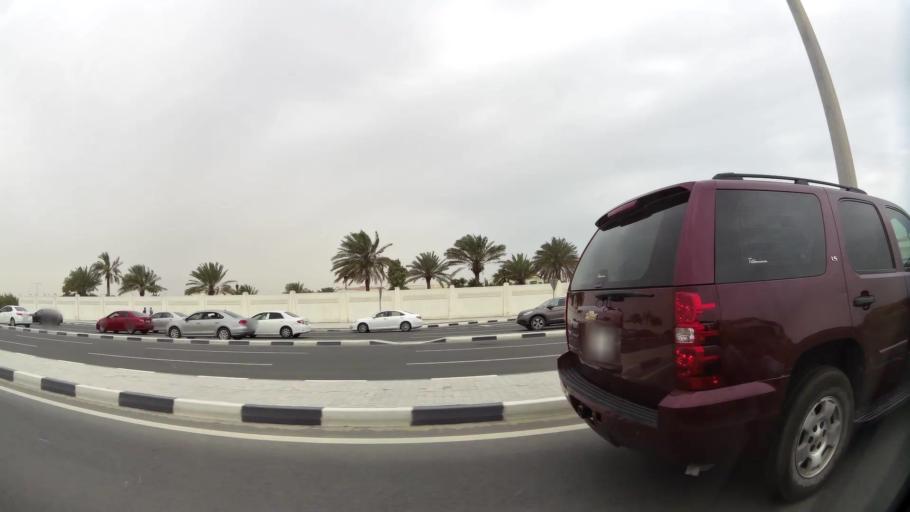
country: QA
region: Baladiyat ar Rayyan
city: Ar Rayyan
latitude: 25.3490
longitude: 51.4805
